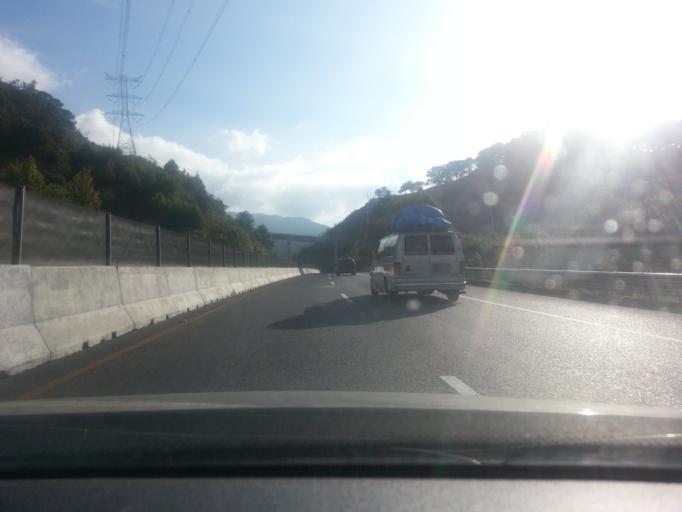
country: MX
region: Puebla
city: Necaxa
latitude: 20.2515
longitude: -98.0281
